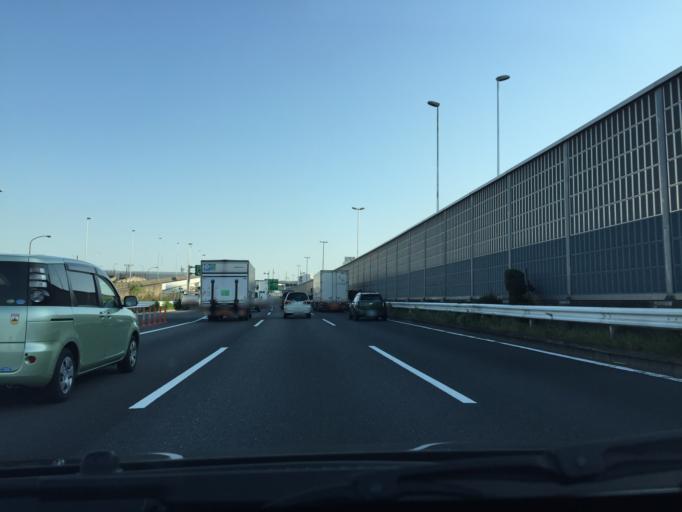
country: JP
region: Kanagawa
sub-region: Kawasaki-shi
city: Kawasaki
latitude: 35.5981
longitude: 139.7553
